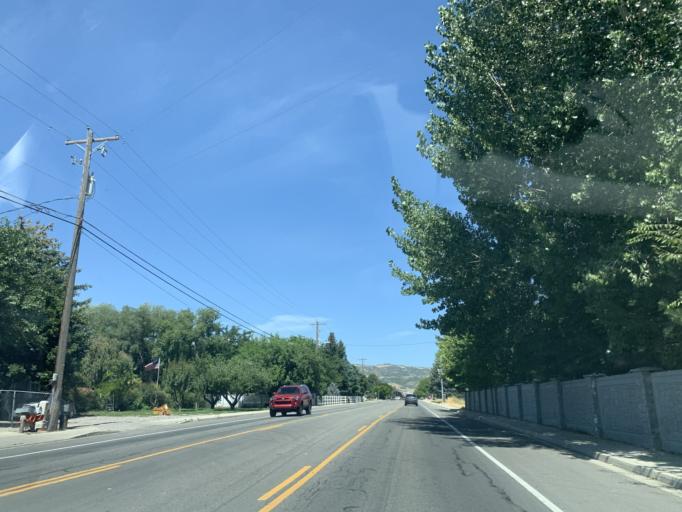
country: US
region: Utah
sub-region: Utah County
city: Lehi
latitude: 40.4093
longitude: -111.8302
